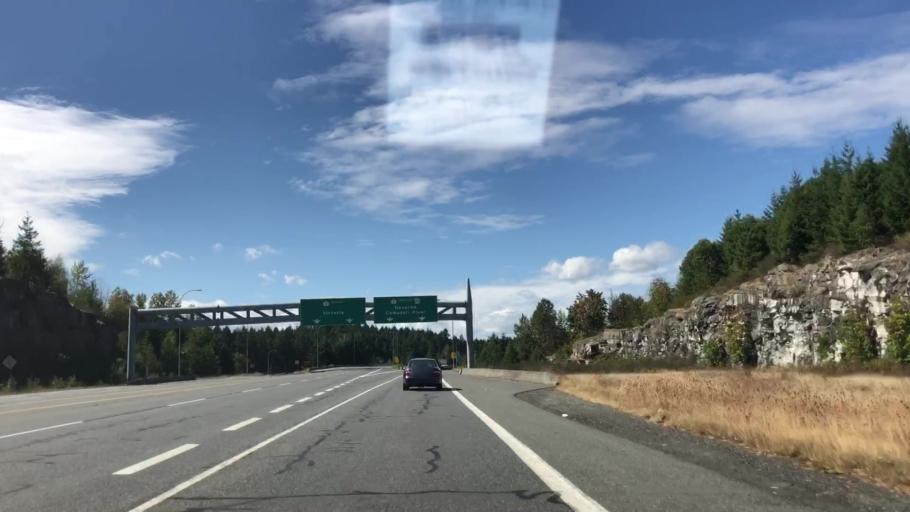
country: CA
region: British Columbia
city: Nanaimo
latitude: 49.1121
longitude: -123.8963
